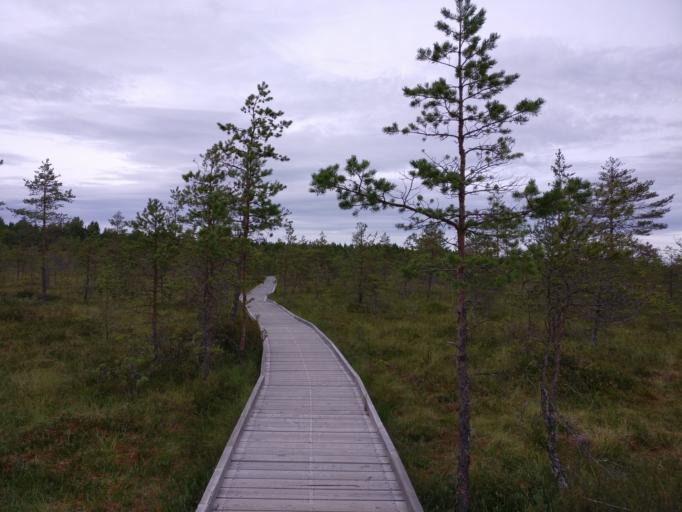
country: EE
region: Paernumaa
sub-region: Vaendra vald (alev)
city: Vandra
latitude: 58.4892
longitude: 24.9824
